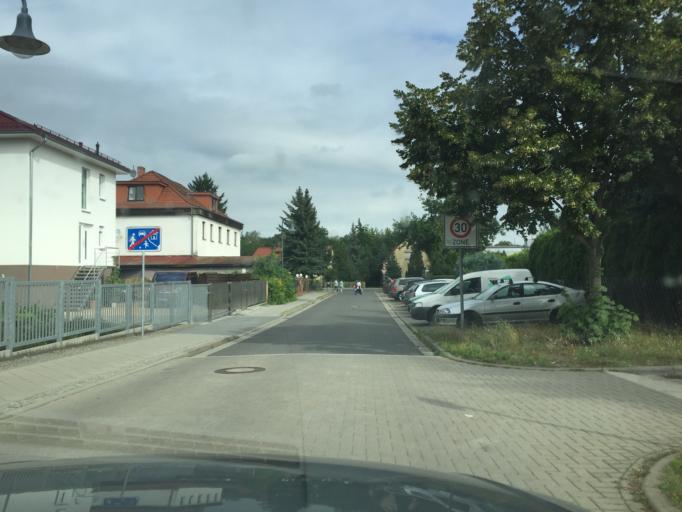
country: DE
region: Brandenburg
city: Erkner
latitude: 52.4203
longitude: 13.7516
